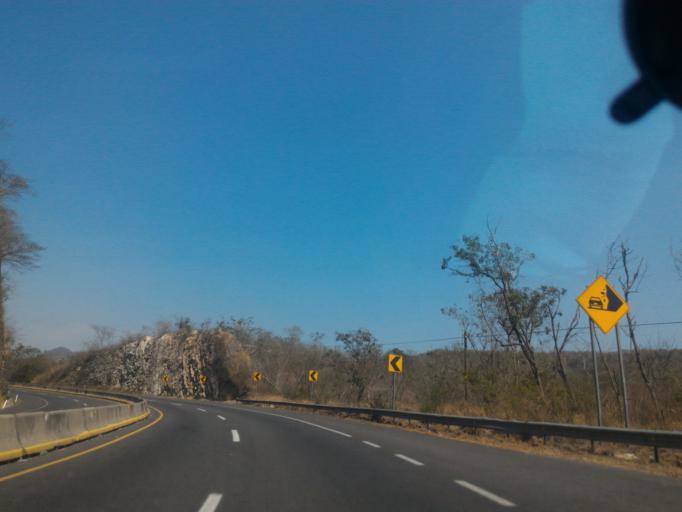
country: MX
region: Colima
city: Ixtlahuacan
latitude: 19.0270
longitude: -103.7952
